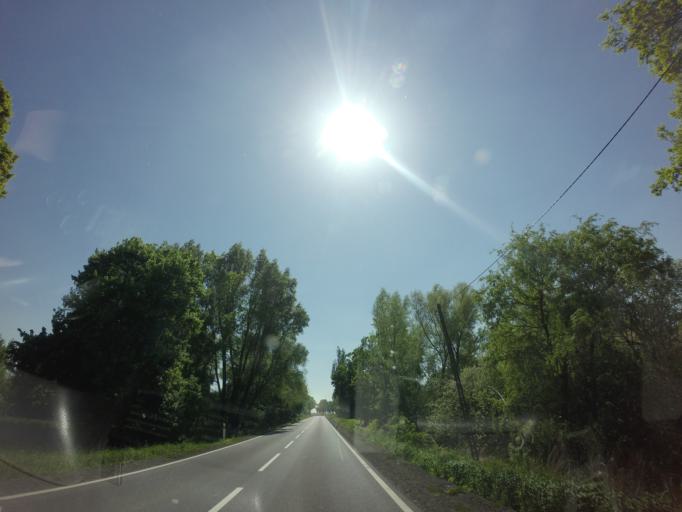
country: PL
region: West Pomeranian Voivodeship
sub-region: Powiat pyrzycki
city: Lipiany
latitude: 52.9961
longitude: 14.9805
